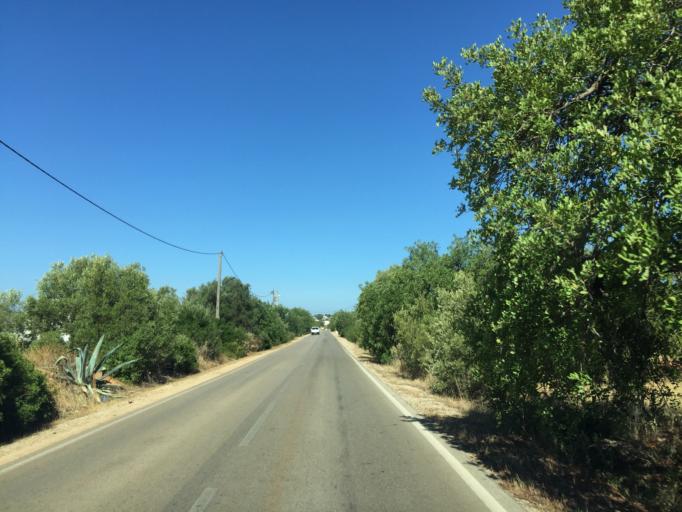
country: PT
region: Faro
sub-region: Loule
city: Almancil
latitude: 37.1106
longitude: -8.0704
